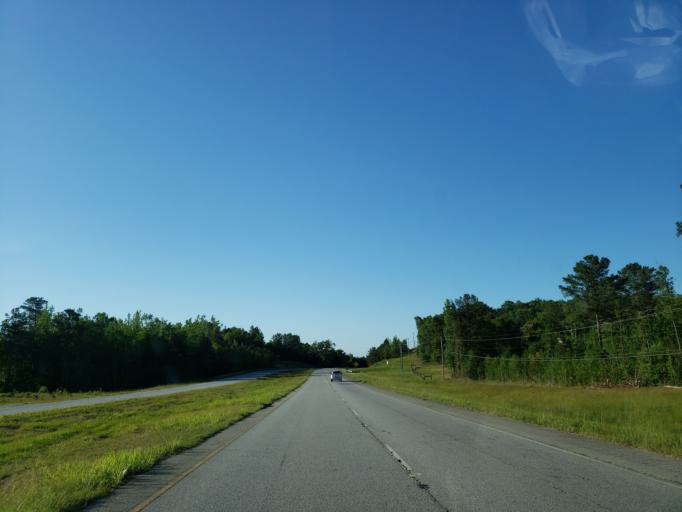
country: US
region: Georgia
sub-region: Polk County
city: Cedartown
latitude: 33.9332
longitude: -85.2467
